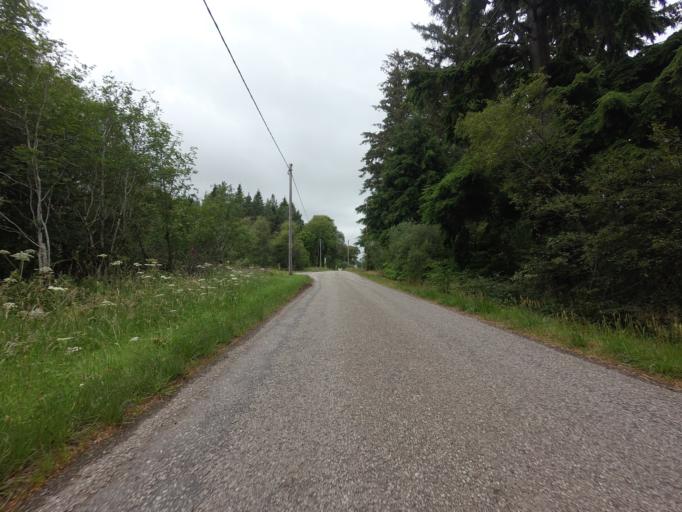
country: GB
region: Scotland
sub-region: Highland
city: Alness
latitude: 57.9929
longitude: -4.4106
